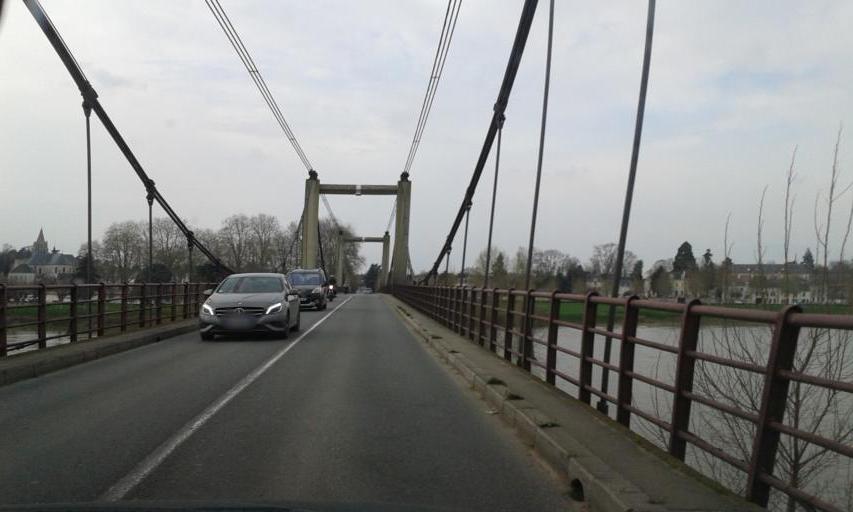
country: FR
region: Centre
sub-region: Departement du Loiret
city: Meung-sur-Loire
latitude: 47.8223
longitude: 1.7030
